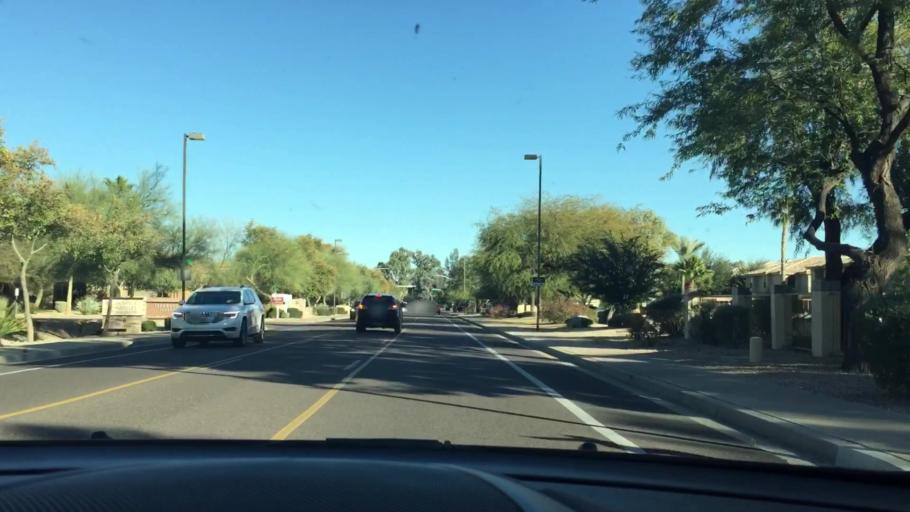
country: US
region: Arizona
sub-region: Maricopa County
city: Scottsdale
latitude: 33.5753
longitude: -111.8767
